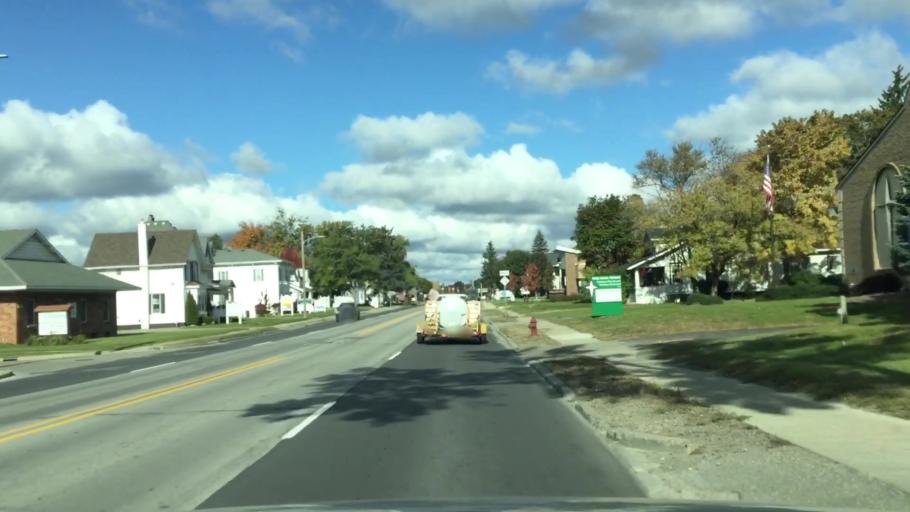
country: US
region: Michigan
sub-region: Oakland County
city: Oxford
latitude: 42.8191
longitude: -83.2598
